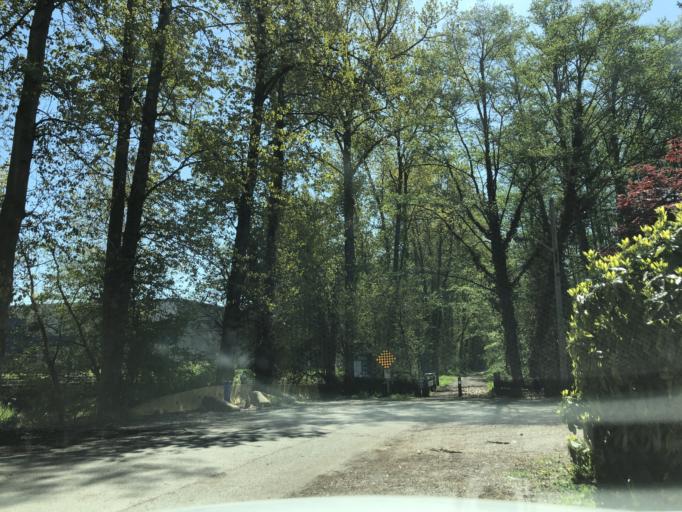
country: CA
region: British Columbia
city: Ladner
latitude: 49.1258
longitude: -123.1033
